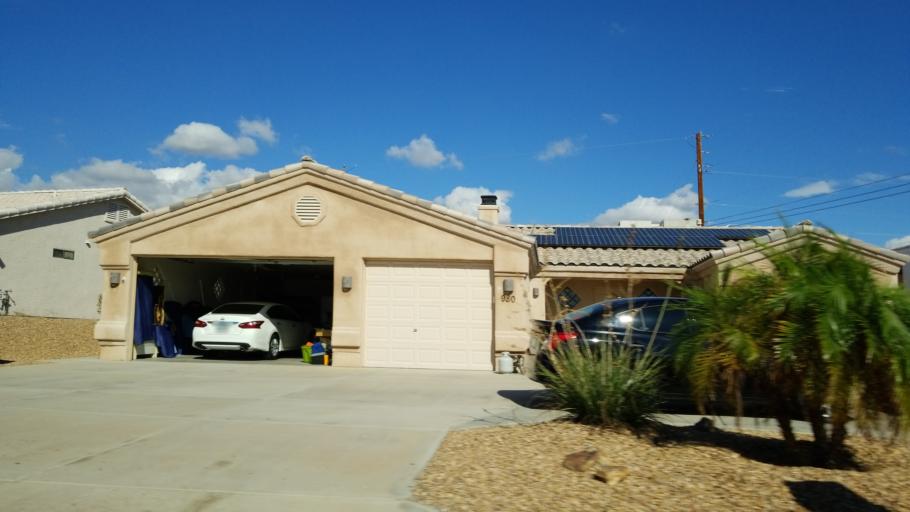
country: US
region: Arizona
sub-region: Mohave County
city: Lake Havasu City
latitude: 34.4761
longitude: -114.2667
